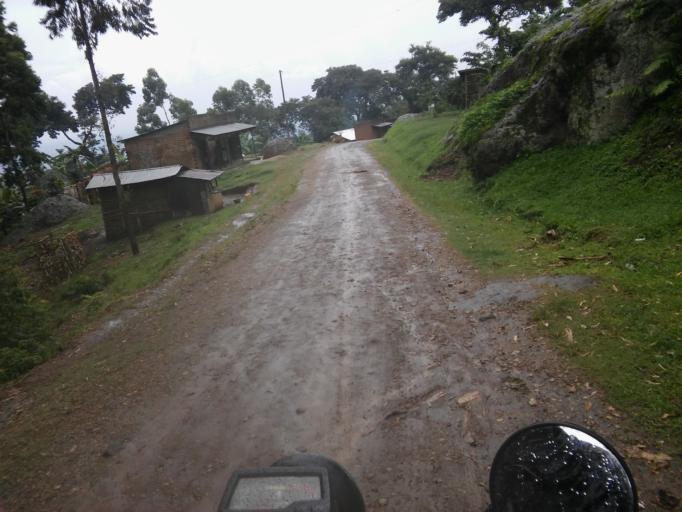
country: UG
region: Eastern Region
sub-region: Mbale District
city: Mbale
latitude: 1.0109
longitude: 34.2318
